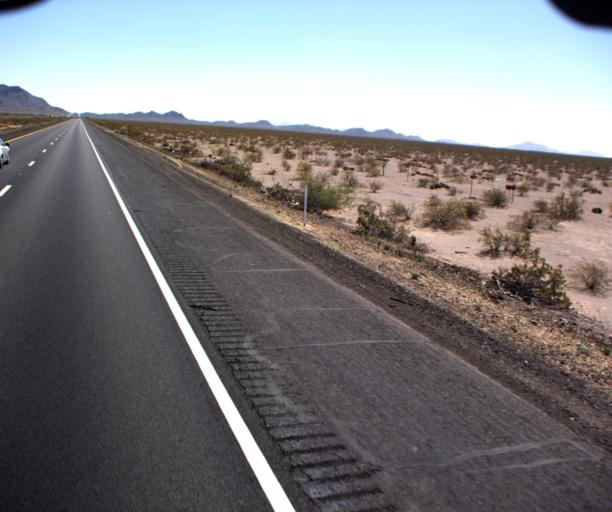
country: US
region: Arizona
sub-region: La Paz County
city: Salome
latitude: 33.6201
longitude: -113.6963
